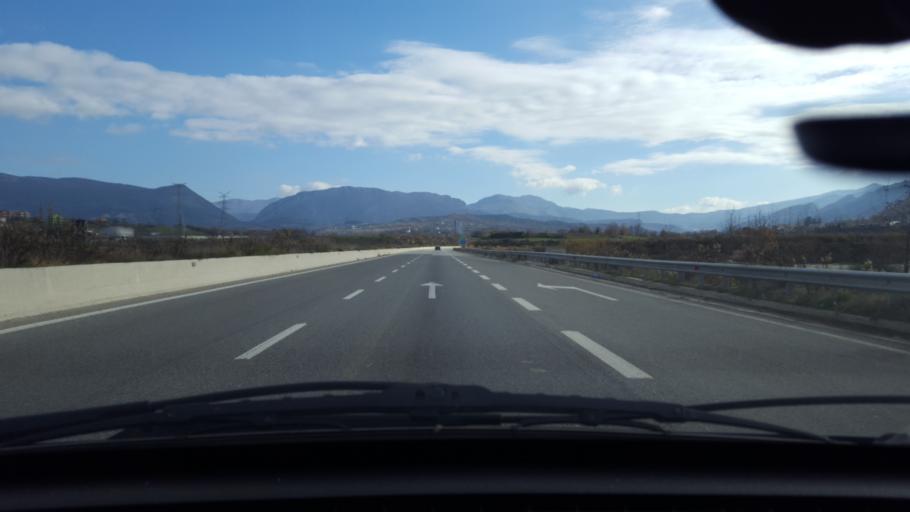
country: AL
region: Tirane
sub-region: Rrethi i Tiranes
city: Berzhite
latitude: 41.2616
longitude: 19.8822
